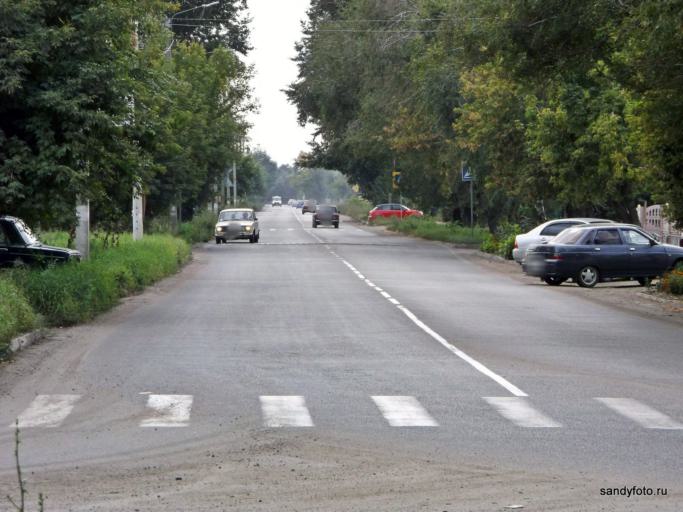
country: RU
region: Chelyabinsk
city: Troitsk
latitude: 54.1113
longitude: 61.5688
